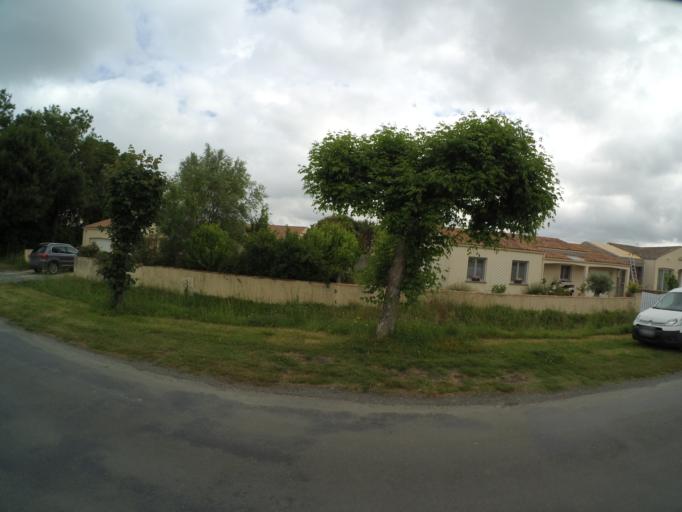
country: FR
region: Poitou-Charentes
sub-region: Departement de la Charente-Maritime
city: Saint-Laurent-de-la-Pree
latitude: 45.9908
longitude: -1.0211
